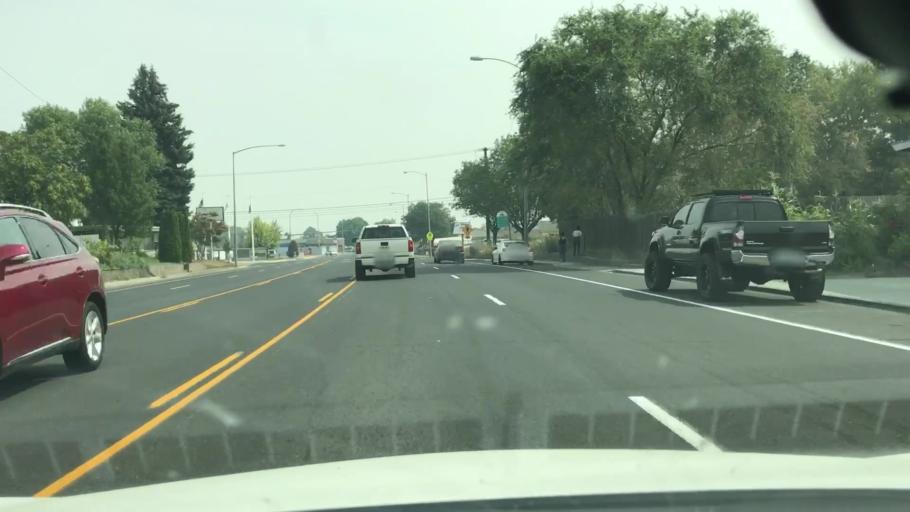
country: US
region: Washington
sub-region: Grant County
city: Quincy
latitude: 47.2335
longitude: -119.8514
